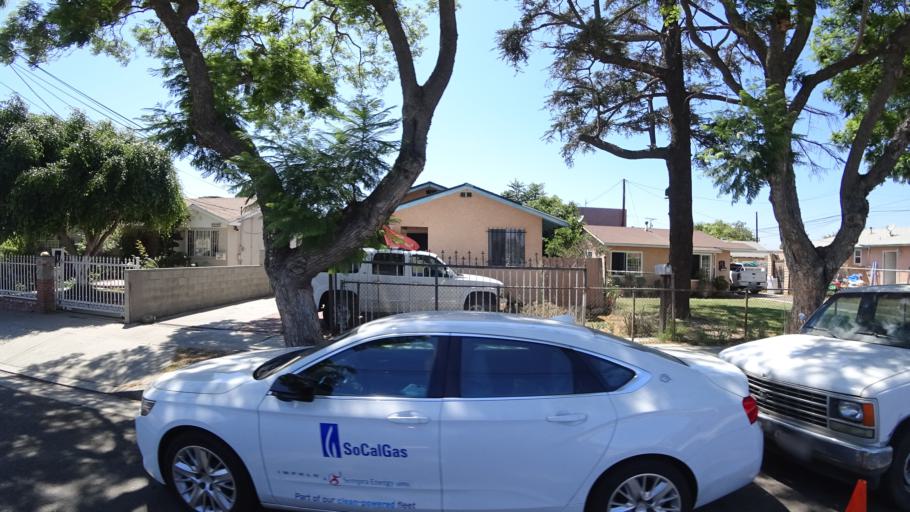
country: US
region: California
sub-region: Los Angeles County
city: Lennox
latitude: 33.9395
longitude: -118.3398
